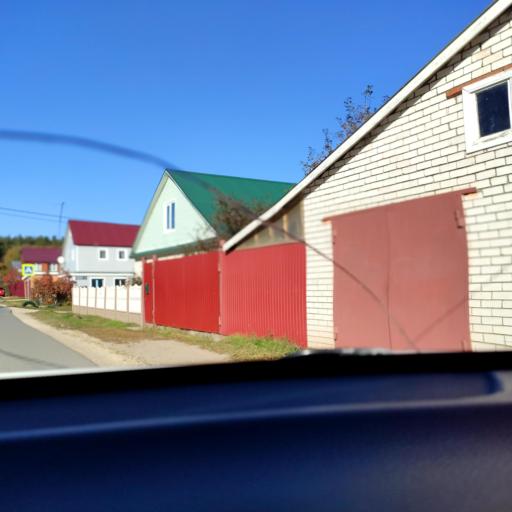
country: RU
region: Tatarstan
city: Vysokaya Gora
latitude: 55.8509
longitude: 49.2323
